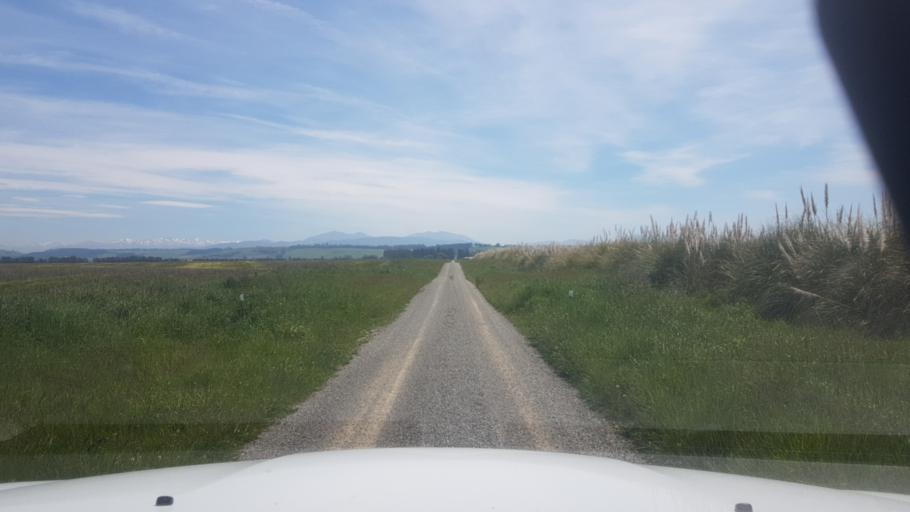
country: NZ
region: Canterbury
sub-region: Timaru District
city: Pleasant Point
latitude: -44.2351
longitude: 171.1682
